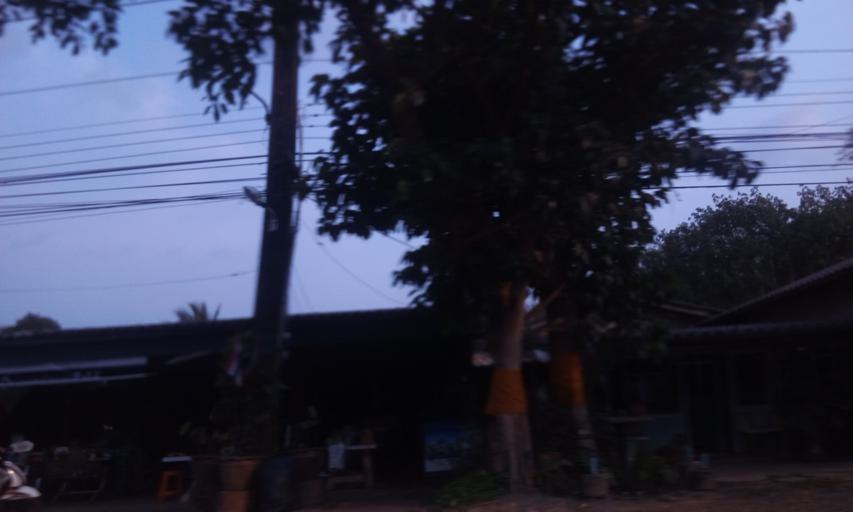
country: TH
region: Trat
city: Khao Saming
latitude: 12.3192
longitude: 102.3595
